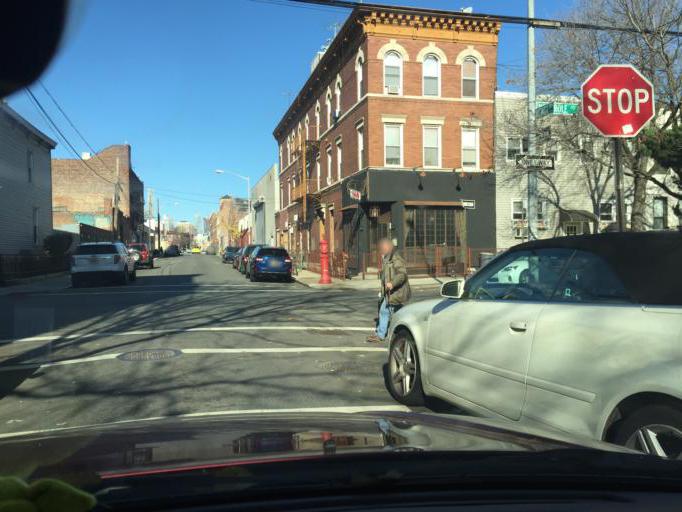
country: US
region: New York
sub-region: Queens County
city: Long Island City
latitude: 40.7281
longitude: -73.9492
